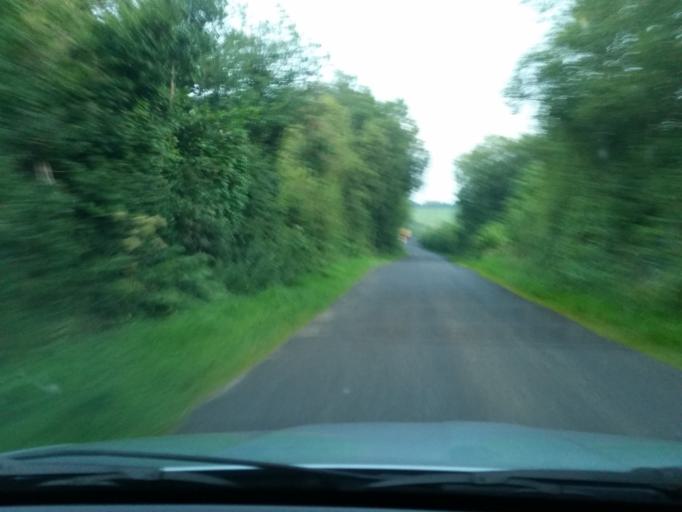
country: GB
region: Northern Ireland
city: Fivemiletown
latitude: 54.3159
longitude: -7.2955
